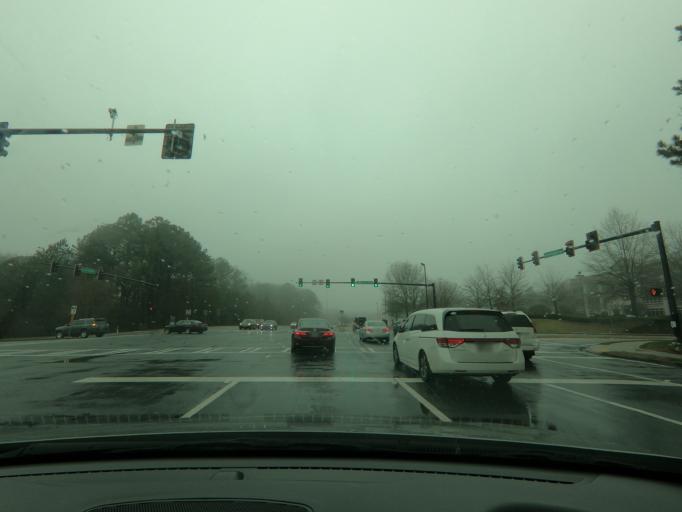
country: US
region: Georgia
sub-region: Fulton County
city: Alpharetta
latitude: 34.0889
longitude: -84.2567
